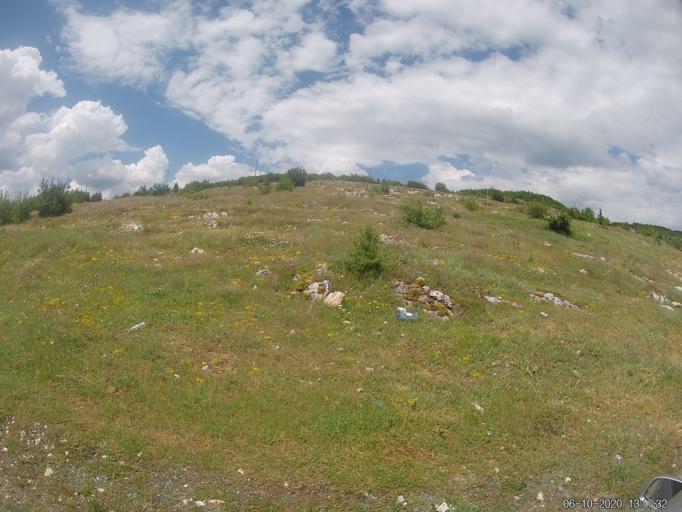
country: XK
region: Prizren
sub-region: Komuna e Therandes
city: Budakovo
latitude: 42.4053
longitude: 20.9174
